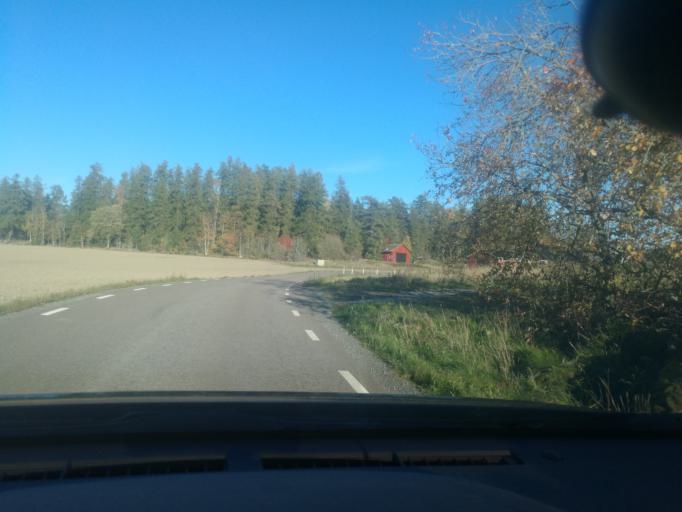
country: SE
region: Vaestmanland
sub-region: Kopings Kommun
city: Koping
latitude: 59.5781
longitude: 16.0014
